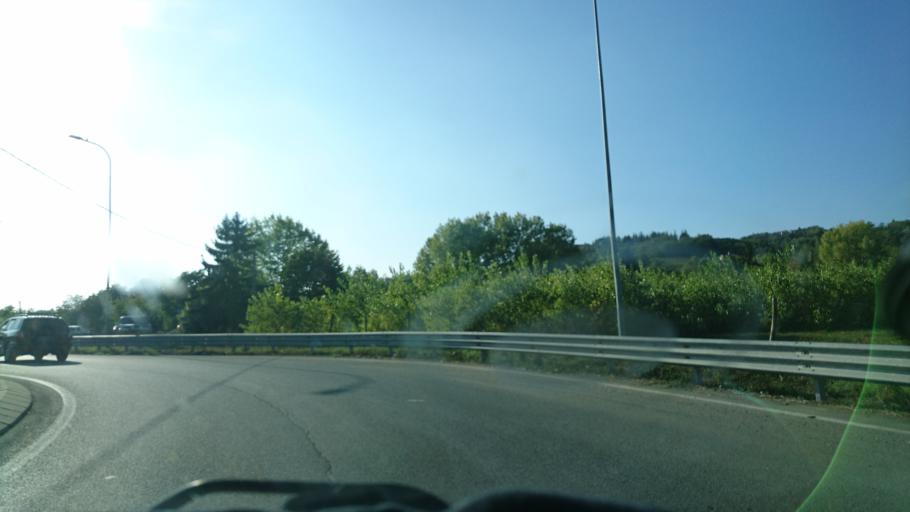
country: IT
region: Piedmont
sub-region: Provincia di Alessandria
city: Visone
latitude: 44.6807
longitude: 8.4963
